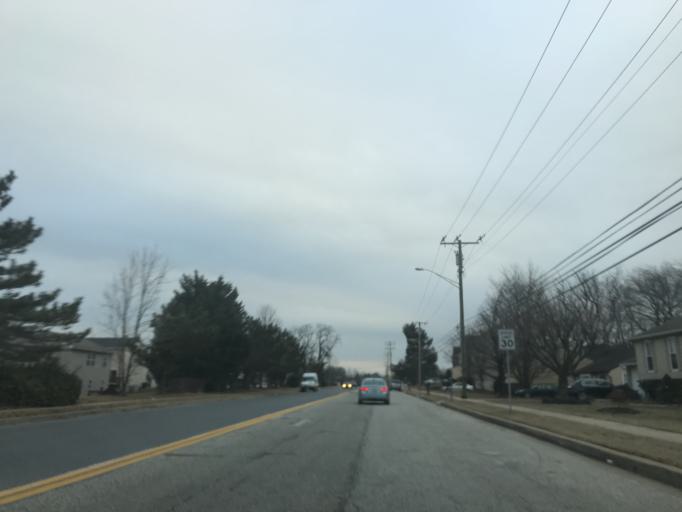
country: US
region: Maryland
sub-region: Baltimore County
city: Randallstown
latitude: 39.3853
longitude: -76.8034
